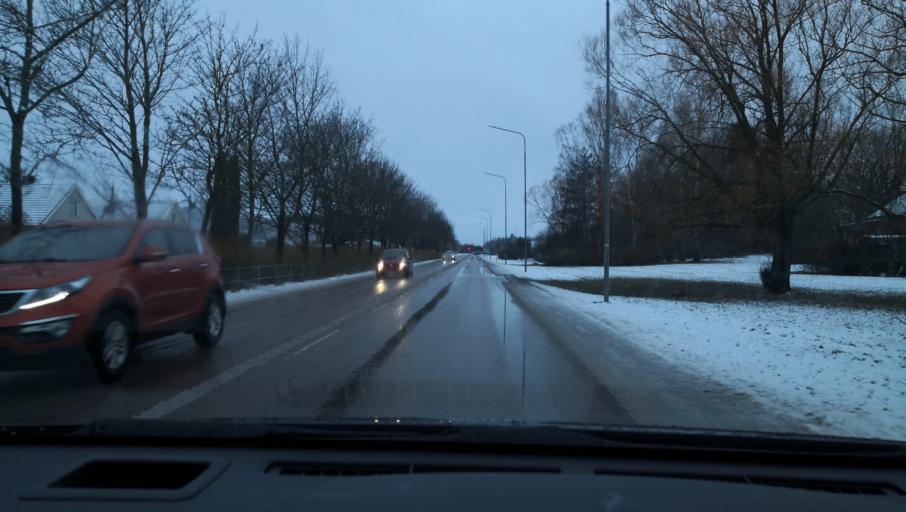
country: SE
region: Vaestmanland
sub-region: Kopings Kommun
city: Koping
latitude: 59.5177
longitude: 16.0102
